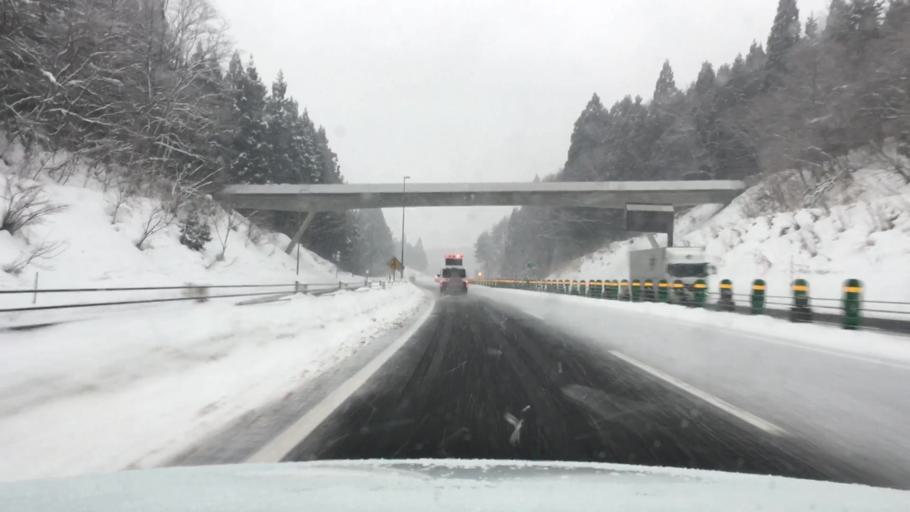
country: JP
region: Akita
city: Hanawa
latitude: 40.1640
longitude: 140.8031
